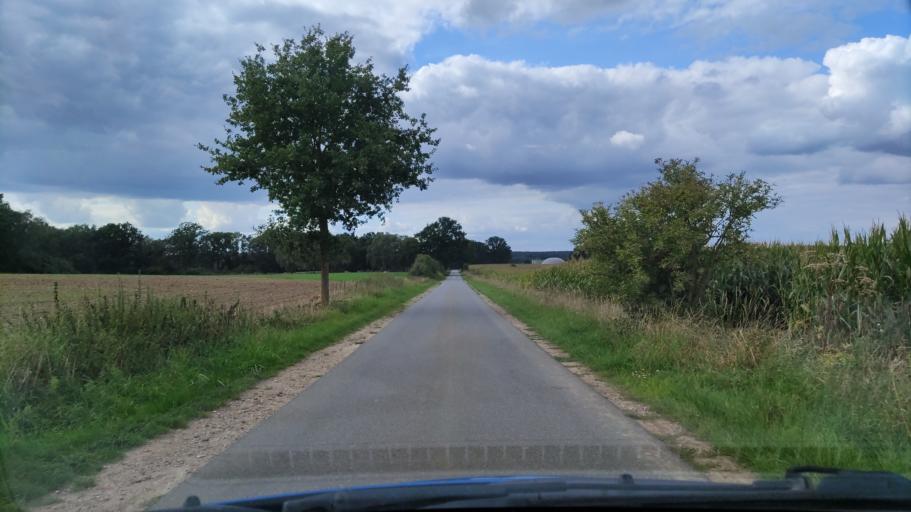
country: DE
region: Lower Saxony
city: Romstedt
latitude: 53.0788
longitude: 10.6558
